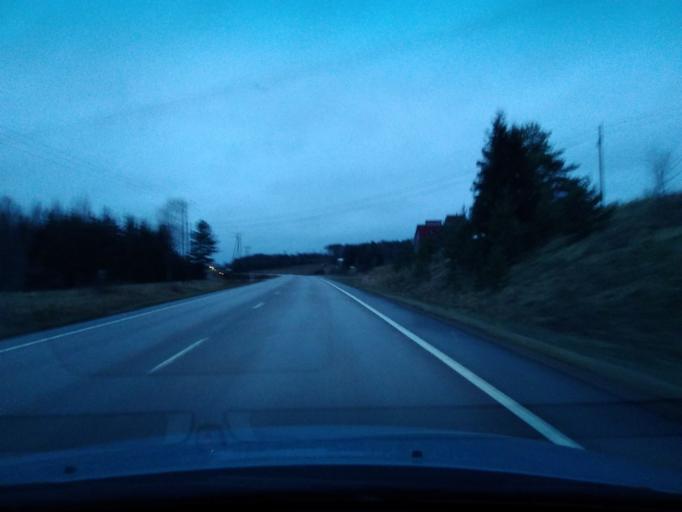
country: FI
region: Uusimaa
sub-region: Porvoo
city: Askola
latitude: 60.4599
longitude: 25.5795
